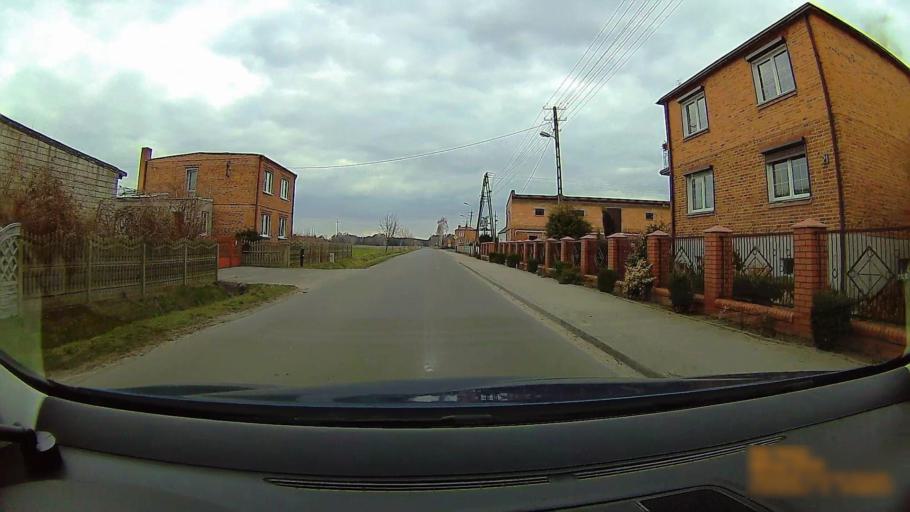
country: PL
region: Greater Poland Voivodeship
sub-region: Powiat koninski
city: Rychwal
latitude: 52.0935
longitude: 18.1405
